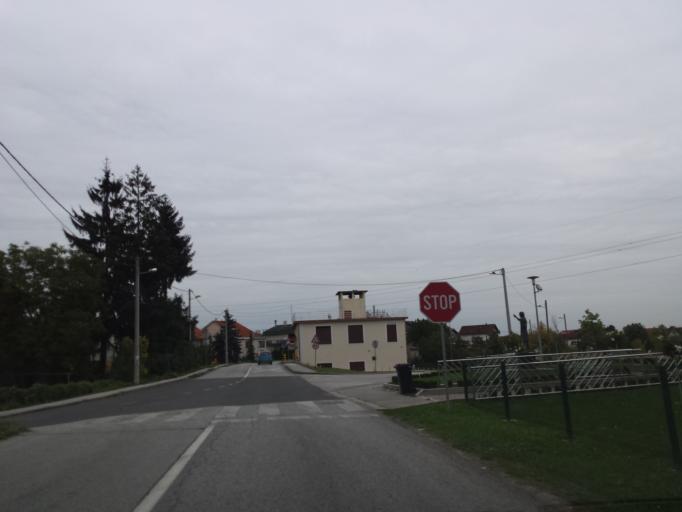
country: HR
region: Grad Zagreb
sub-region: Sesvete
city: Sesvete
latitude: 45.7985
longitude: 16.1182
